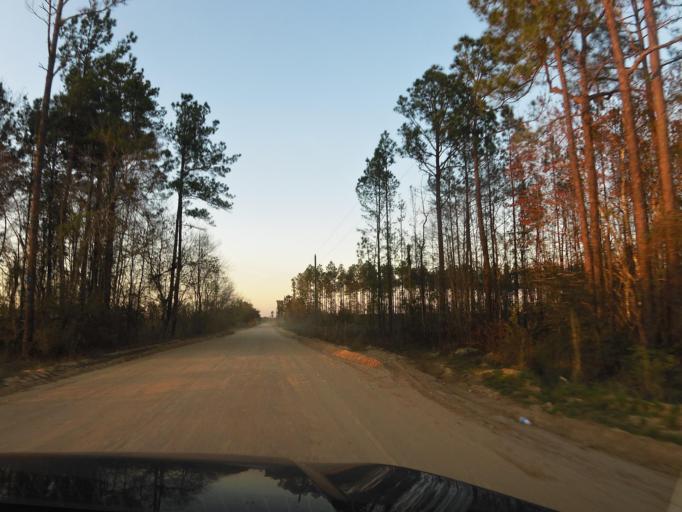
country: US
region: Florida
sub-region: Clay County
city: Green Cove Springs
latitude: 29.9064
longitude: -81.7803
